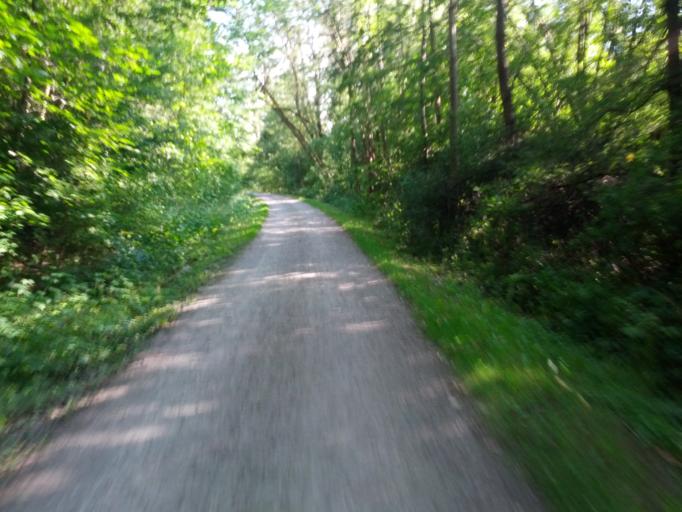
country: DE
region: Thuringia
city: Creuzburg
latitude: 51.0697
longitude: 10.2680
